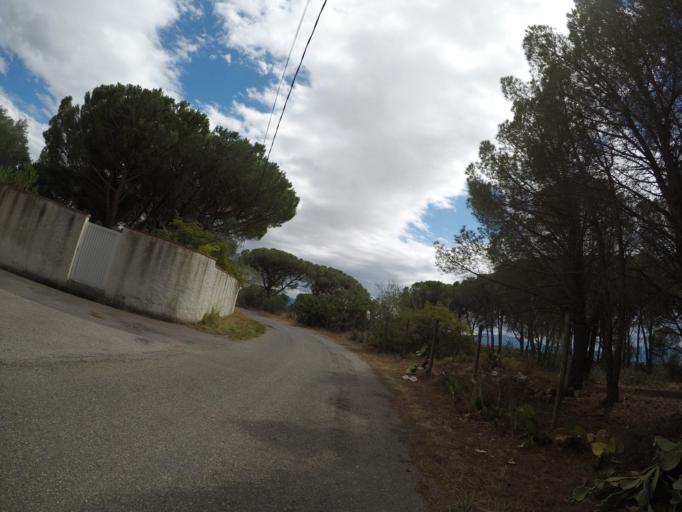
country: FR
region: Languedoc-Roussillon
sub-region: Departement des Pyrenees-Orientales
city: Baho
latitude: 42.7093
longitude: 2.8174
